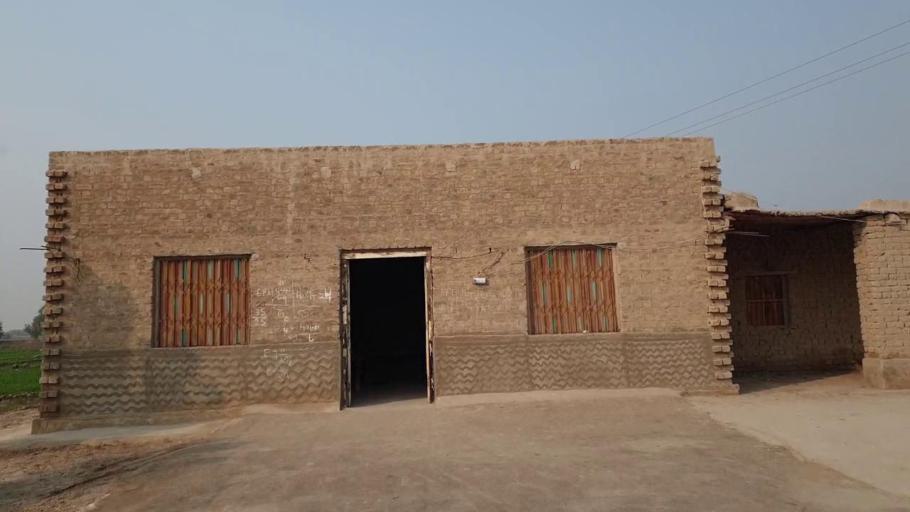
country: PK
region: Sindh
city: Bhan
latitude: 26.4641
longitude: 67.7101
